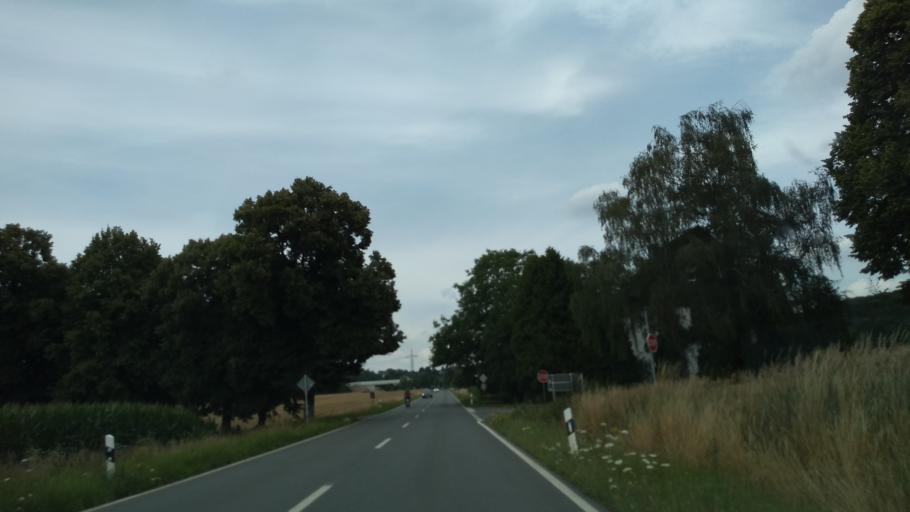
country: DE
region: North Rhine-Westphalia
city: Schwerte
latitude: 51.4661
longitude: 7.6047
